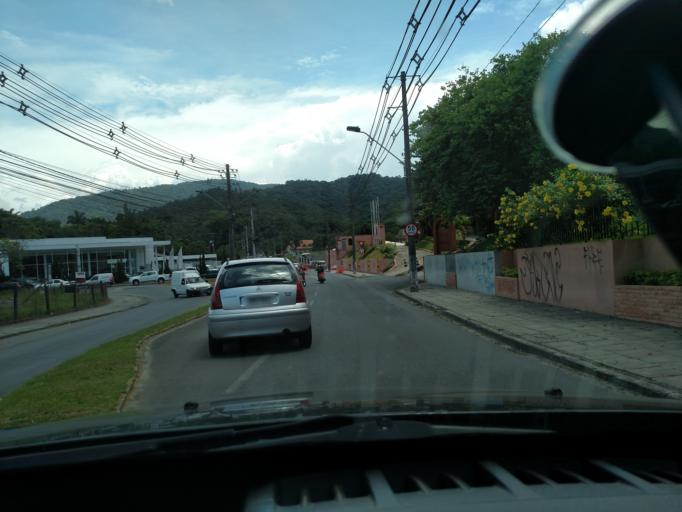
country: BR
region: Santa Catarina
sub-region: Blumenau
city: Blumenau
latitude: -26.9353
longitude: -49.0666
